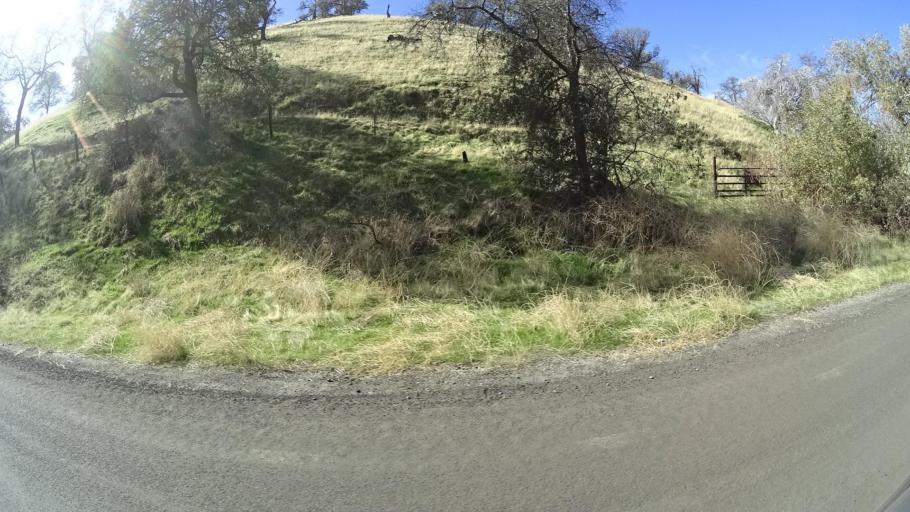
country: US
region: California
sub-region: Kern County
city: Oildale
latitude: 35.6547
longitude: -118.8410
